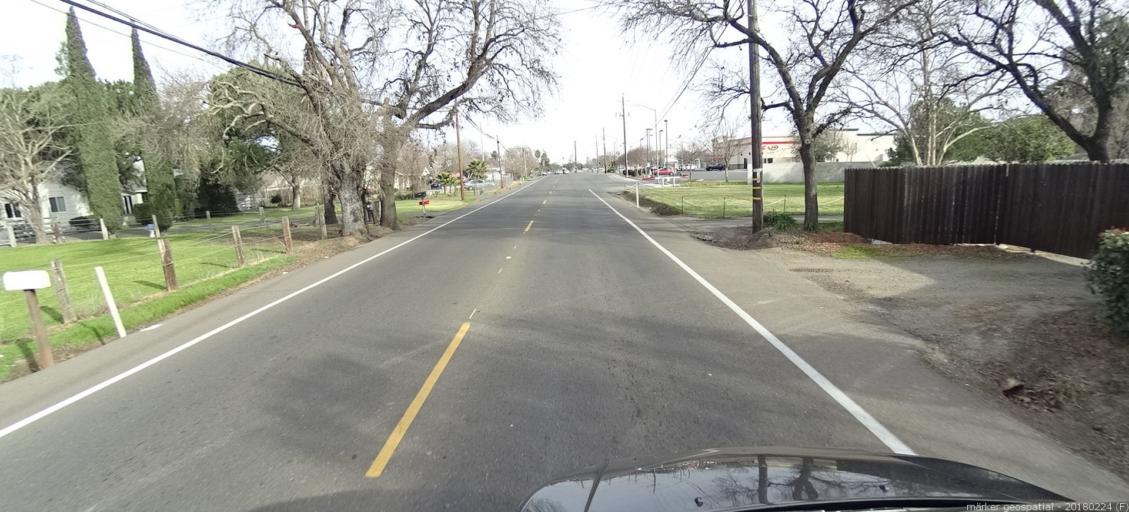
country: US
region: California
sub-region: Sacramento County
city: Rio Linda
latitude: 38.6816
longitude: -121.4569
